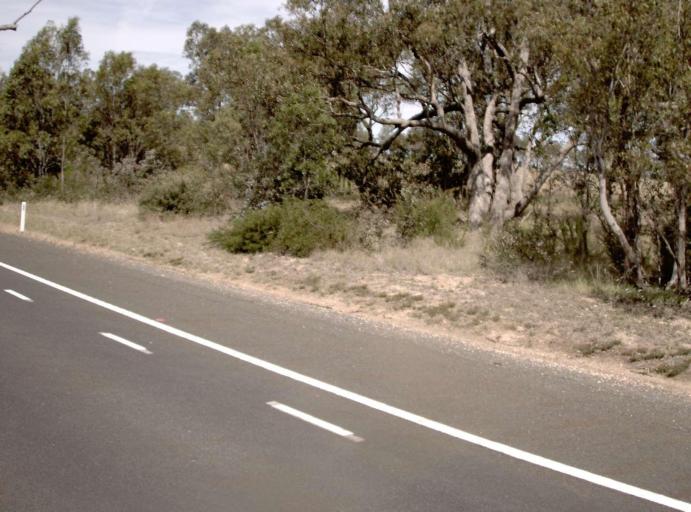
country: AU
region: Victoria
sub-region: East Gippsland
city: Bairnsdale
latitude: -37.8917
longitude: 147.3823
